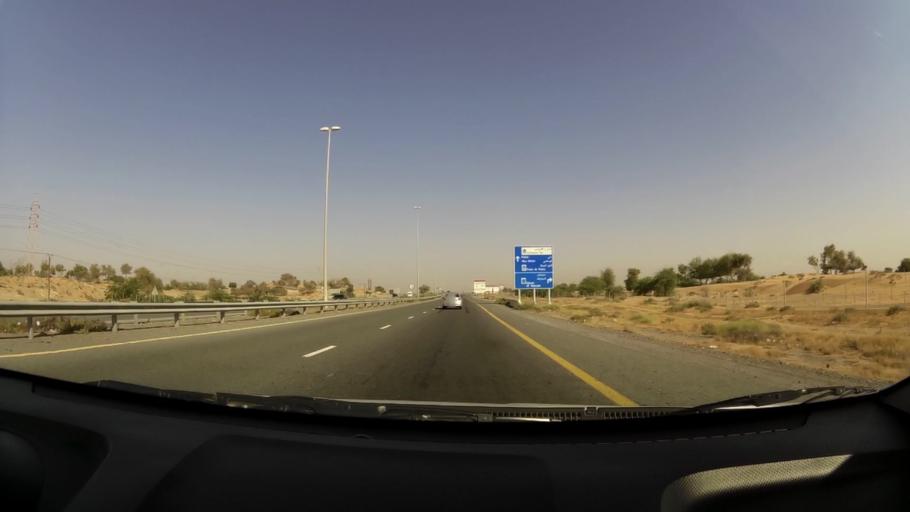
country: AE
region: Umm al Qaywayn
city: Umm al Qaywayn
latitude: 25.4579
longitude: 55.6073
